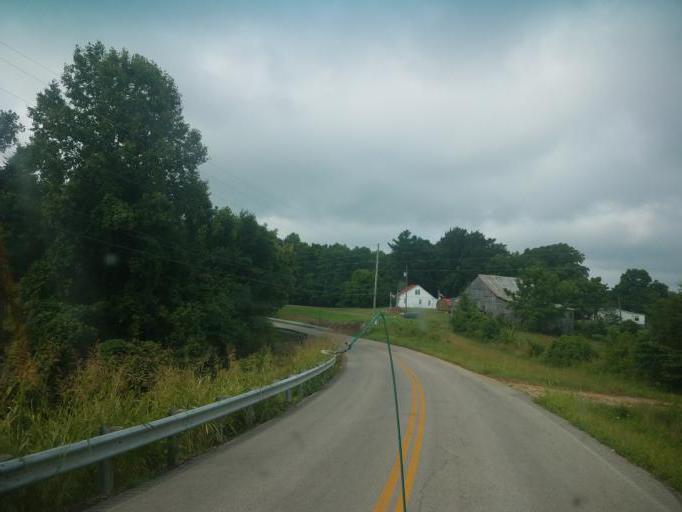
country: US
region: Kentucky
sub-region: Clinton County
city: Albany
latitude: 36.7930
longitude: -85.1475
